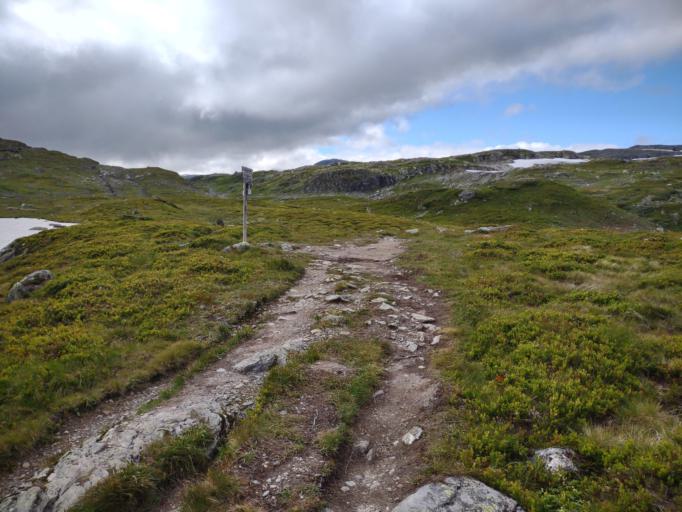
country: NO
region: Aust-Agder
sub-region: Bykle
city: Hovden
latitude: 59.8385
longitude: 7.2086
